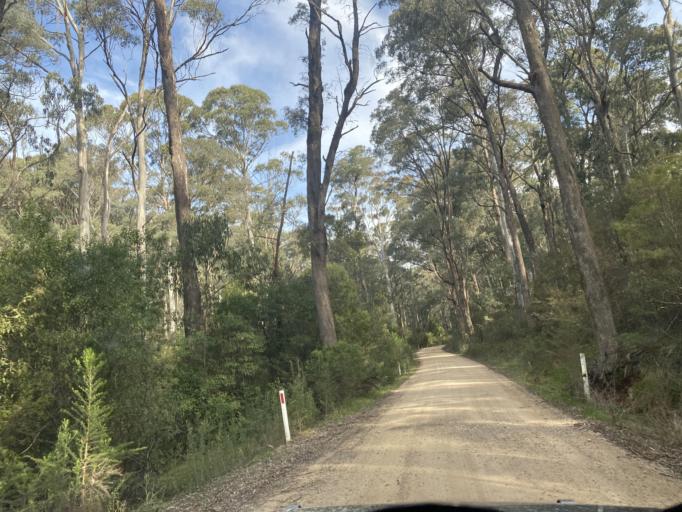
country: AU
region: Victoria
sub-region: Mansfield
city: Mansfield
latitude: -36.8654
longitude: 146.1985
